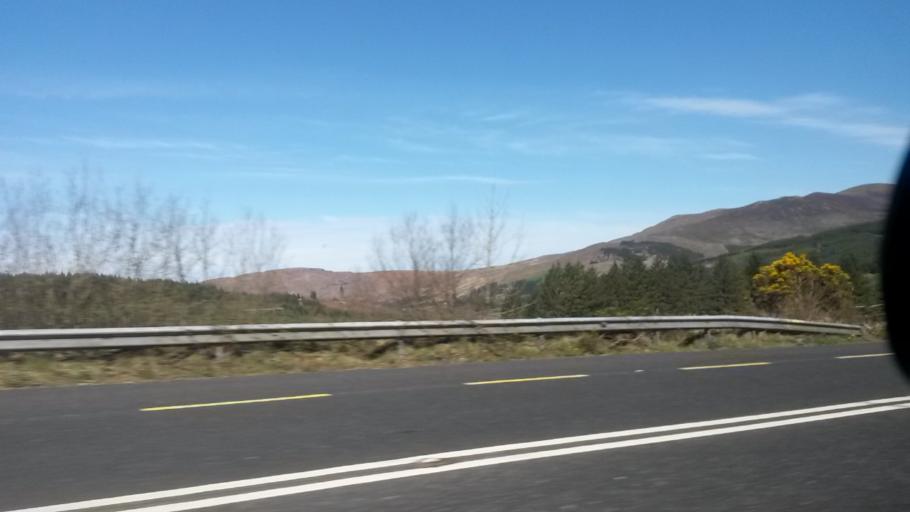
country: IE
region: Munster
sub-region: County Cork
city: Millstreet
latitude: 51.9739
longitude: -9.2523
